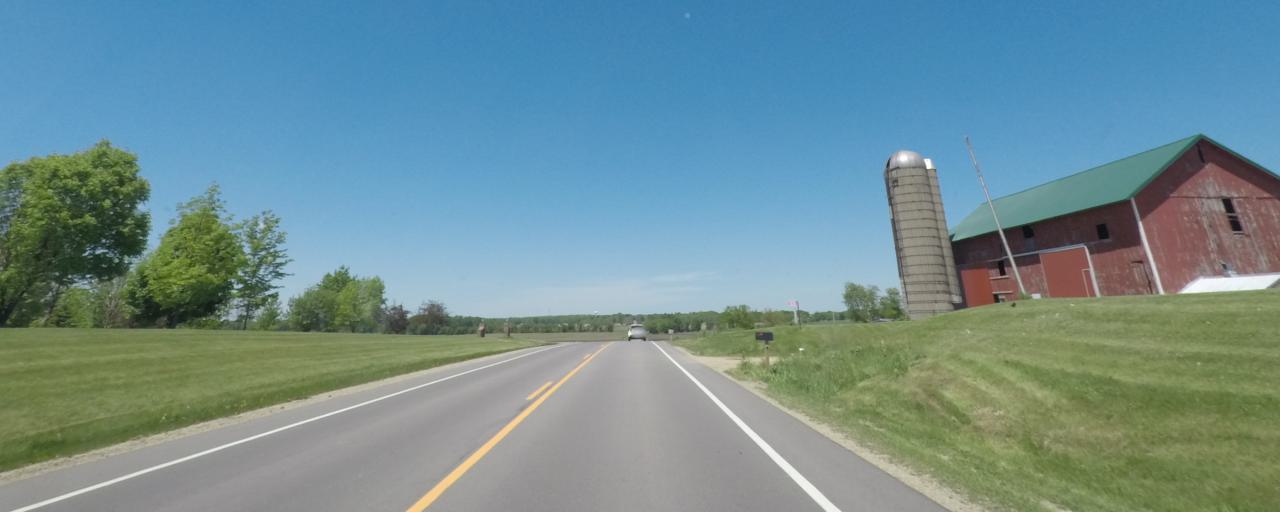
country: US
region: Wisconsin
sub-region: Green County
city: Brooklyn
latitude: 42.8308
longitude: -89.3693
